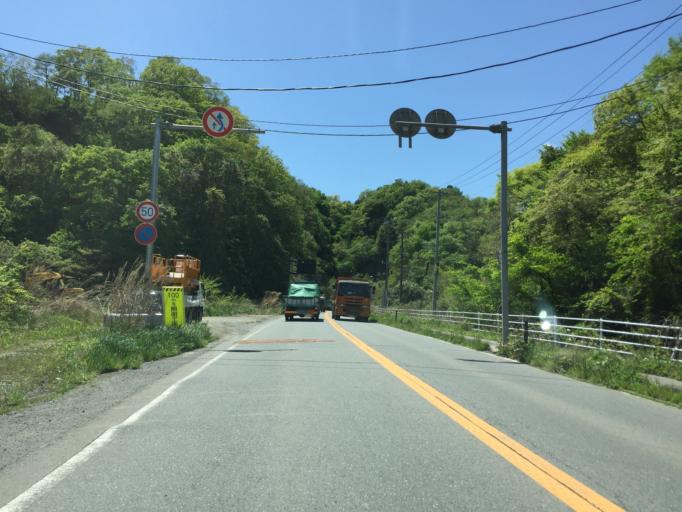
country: JP
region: Fukushima
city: Iwaki
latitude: 36.9614
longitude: 140.8716
